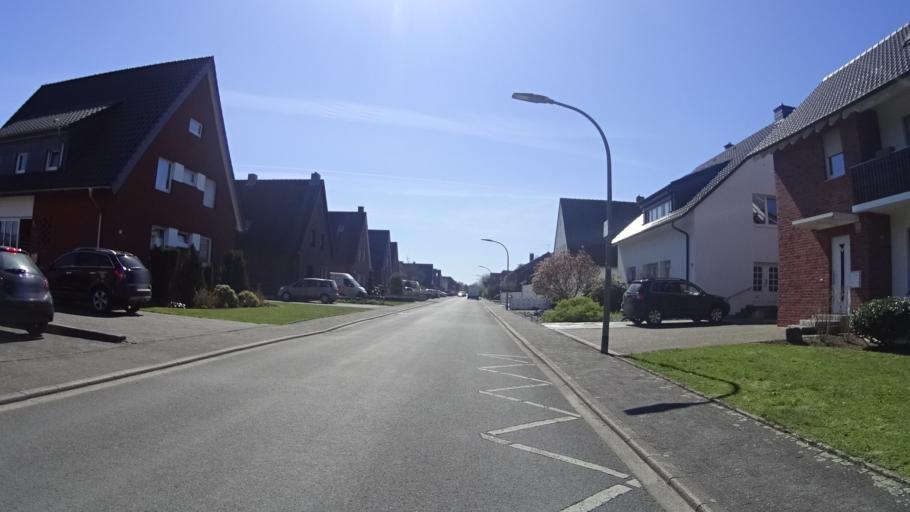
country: DE
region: North Rhine-Westphalia
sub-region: Regierungsbezirk Munster
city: Haltern
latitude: 51.7710
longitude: 7.2244
